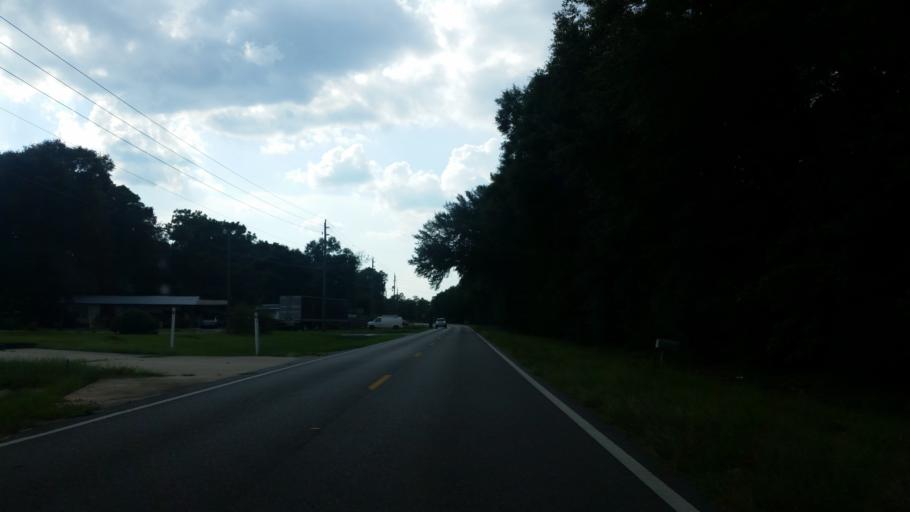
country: US
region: Florida
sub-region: Santa Rosa County
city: Bagdad
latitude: 30.6011
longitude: -87.0579
